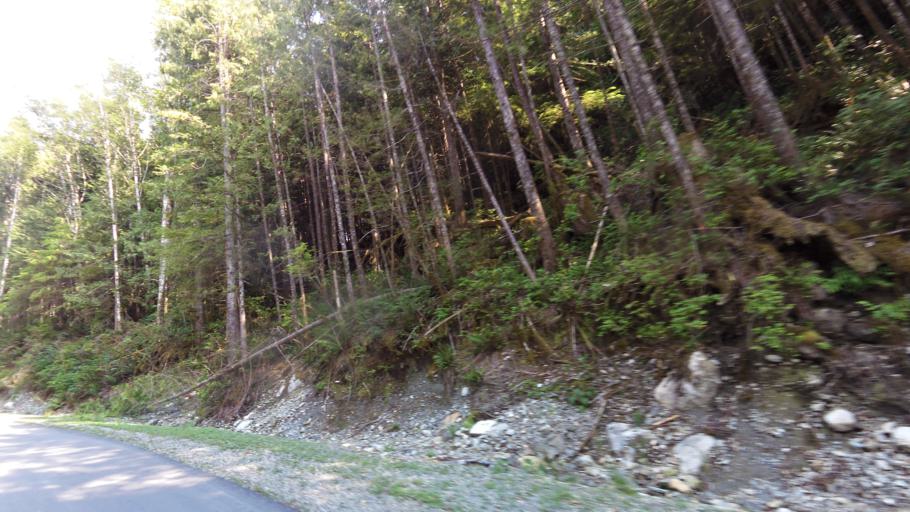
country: CA
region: British Columbia
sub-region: Regional District of Alberni-Clayoquot
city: Tofino
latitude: 49.0855
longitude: -125.8407
